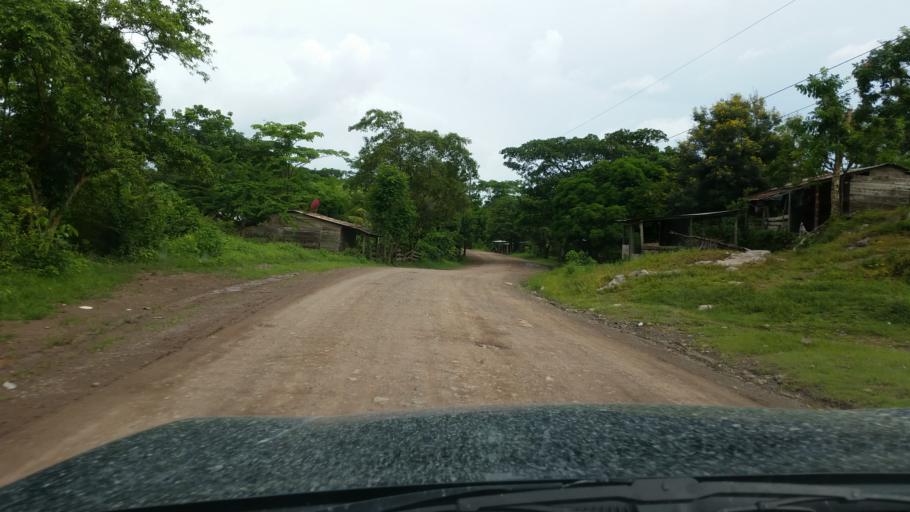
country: NI
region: Atlantico Norte (RAAN)
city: Siuna
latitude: 13.4947
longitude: -84.8445
